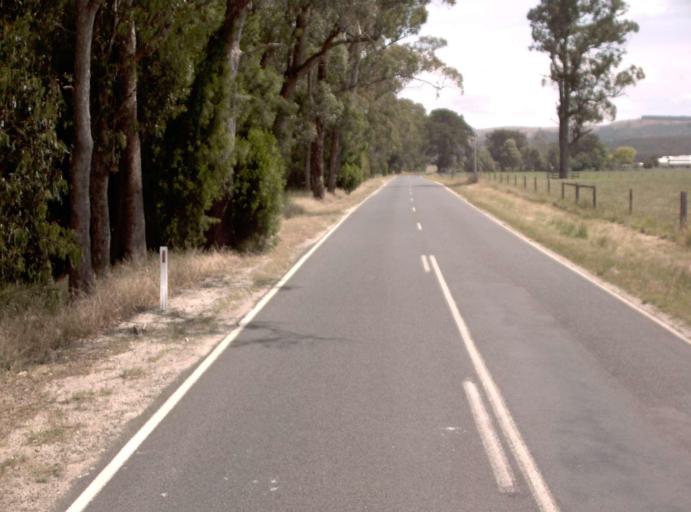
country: AU
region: Victoria
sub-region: Latrobe
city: Traralgon
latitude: -38.2833
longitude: 146.5458
